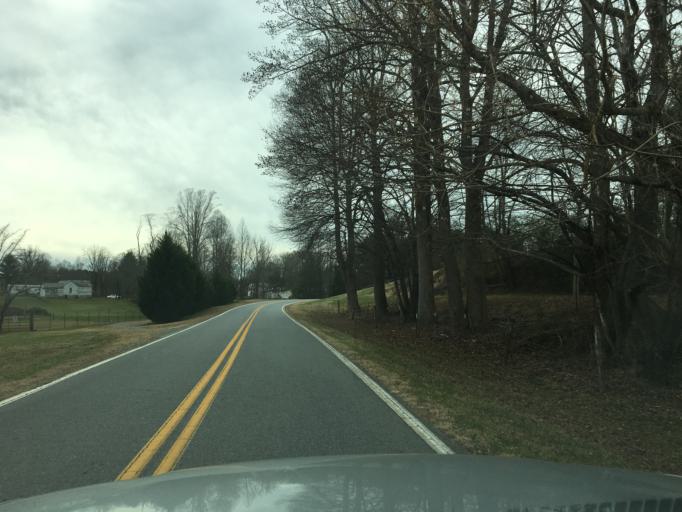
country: US
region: North Carolina
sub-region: McDowell County
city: West Marion
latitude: 35.6175
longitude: -81.9730
